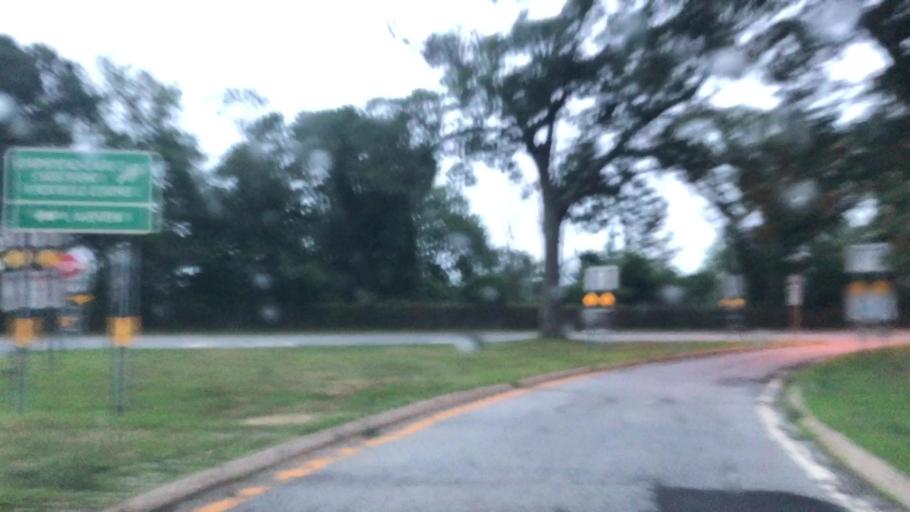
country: US
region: New York
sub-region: Nassau County
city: Lakeview
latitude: 40.6837
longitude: -73.6428
